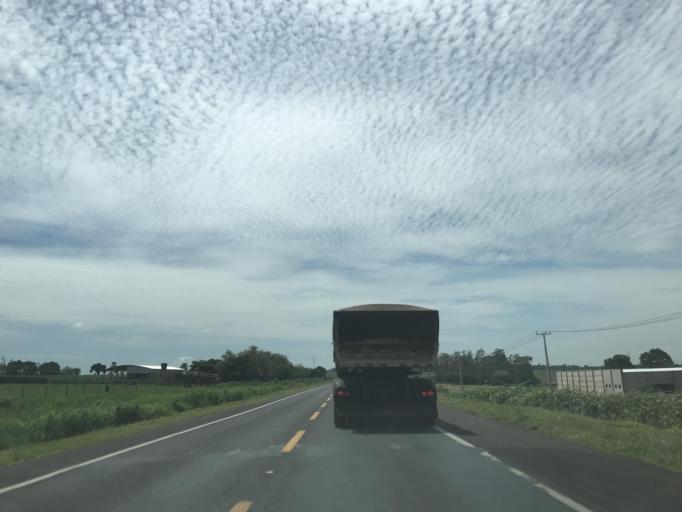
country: BR
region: Parana
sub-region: Paranavai
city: Paranavai
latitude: -23.0149
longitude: -52.5243
